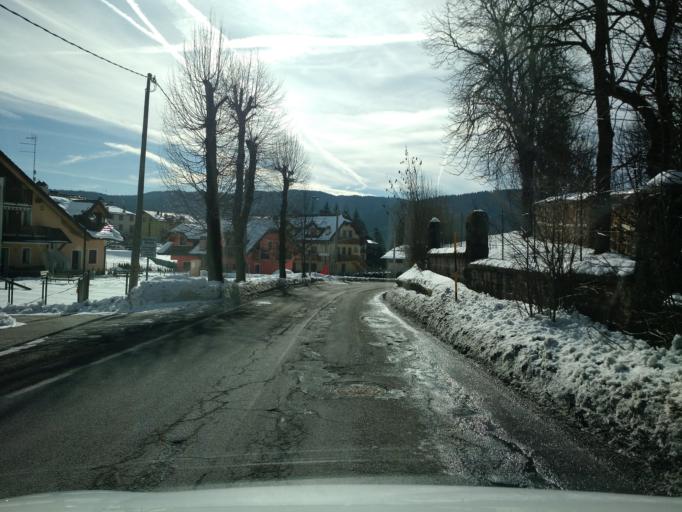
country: IT
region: Veneto
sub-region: Provincia di Vicenza
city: Canove di Roana
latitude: 45.8594
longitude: 11.4722
